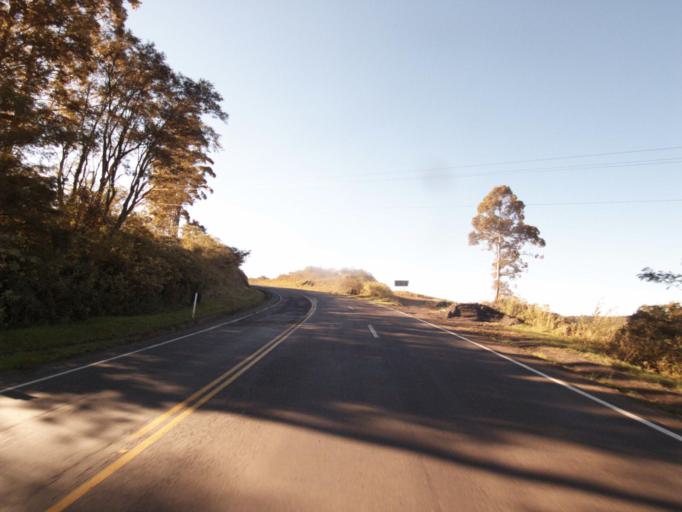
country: AR
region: Misiones
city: Bernardo de Irigoyen
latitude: -26.3304
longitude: -53.5444
